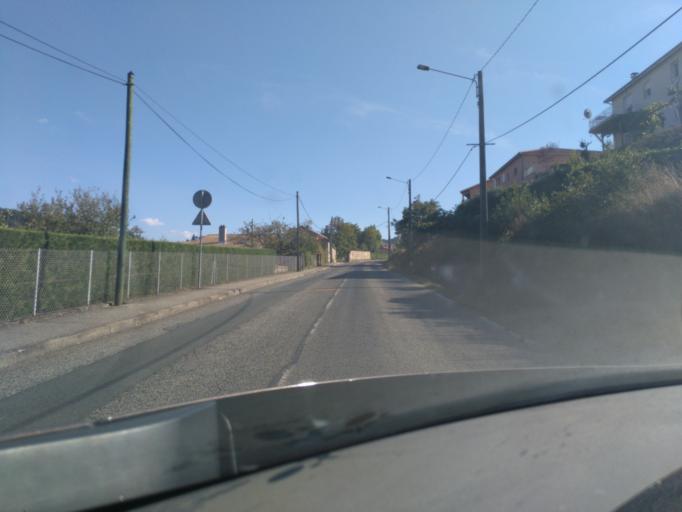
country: FR
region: Rhone-Alpes
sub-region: Departement du Rhone
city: Tarare
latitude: 45.8890
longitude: 4.4345
